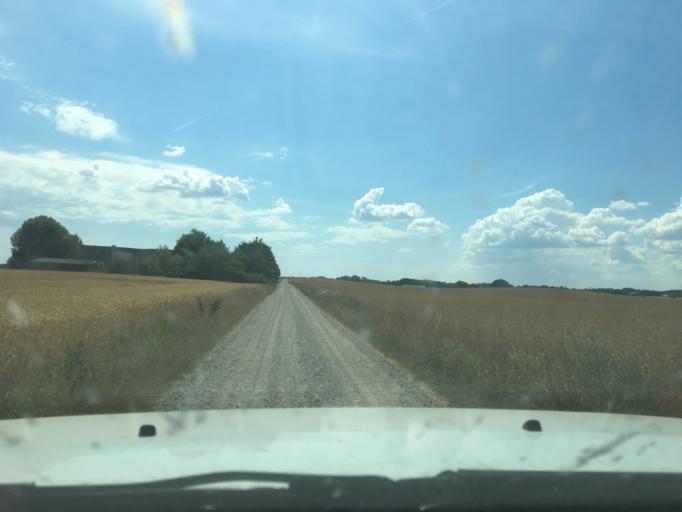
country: DK
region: Central Jutland
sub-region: Randers Kommune
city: Assentoft
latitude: 56.3476
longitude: 10.1879
